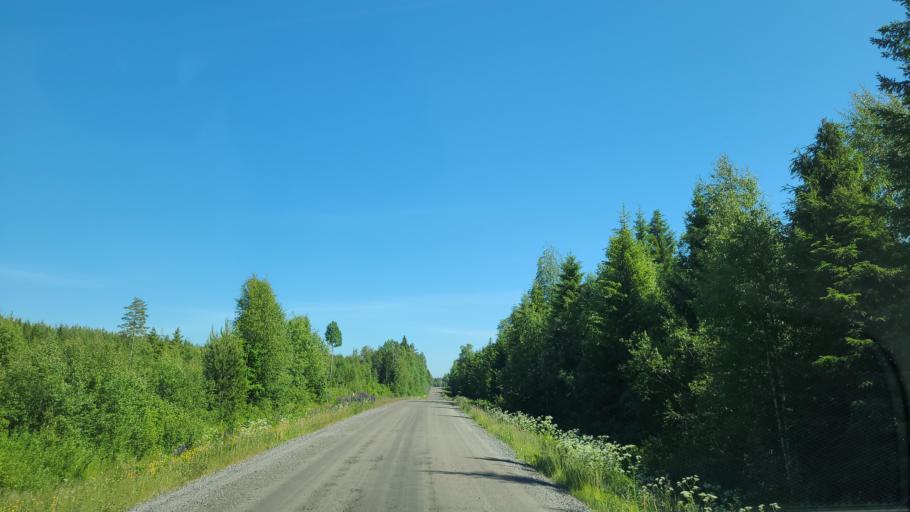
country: SE
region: Vaesterbotten
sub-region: Bjurholms Kommun
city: Bjurholm
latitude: 63.6427
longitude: 19.1243
